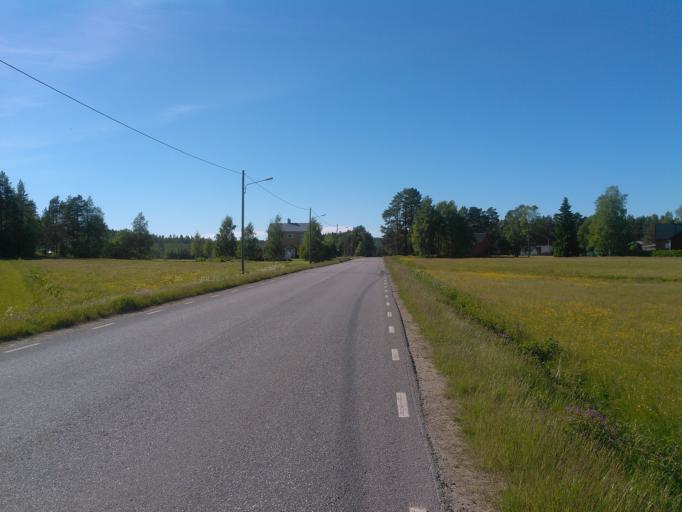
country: SE
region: Vaesterbotten
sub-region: Umea Kommun
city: Roback
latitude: 63.8284
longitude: 20.1168
